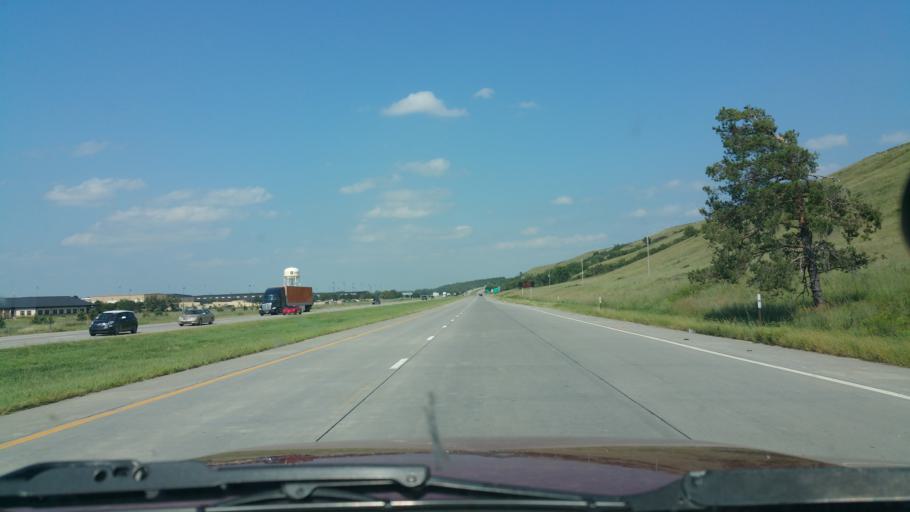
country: US
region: Kansas
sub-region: Geary County
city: Grandview Plaza
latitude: 39.0414
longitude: -96.7638
